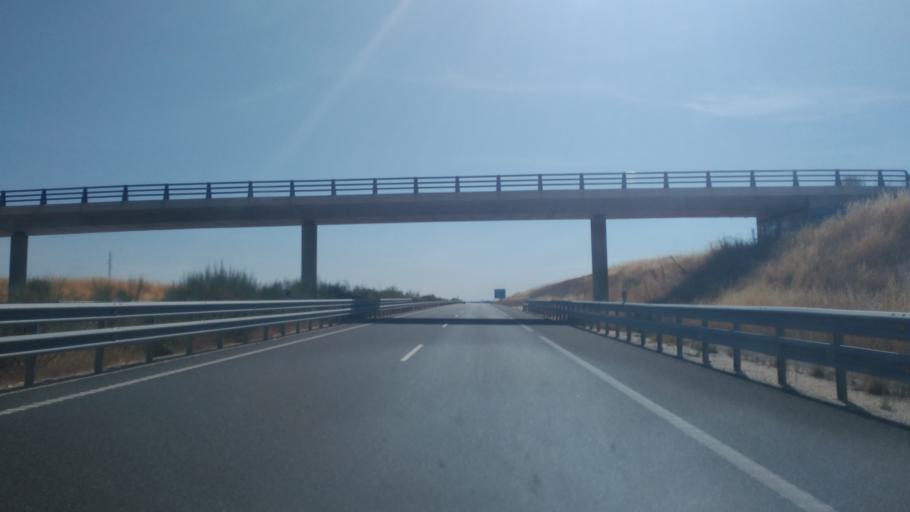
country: ES
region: Castille and Leon
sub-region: Provincia de Salamanca
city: Ventosa del Rio Almar
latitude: 40.9325
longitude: -5.3241
